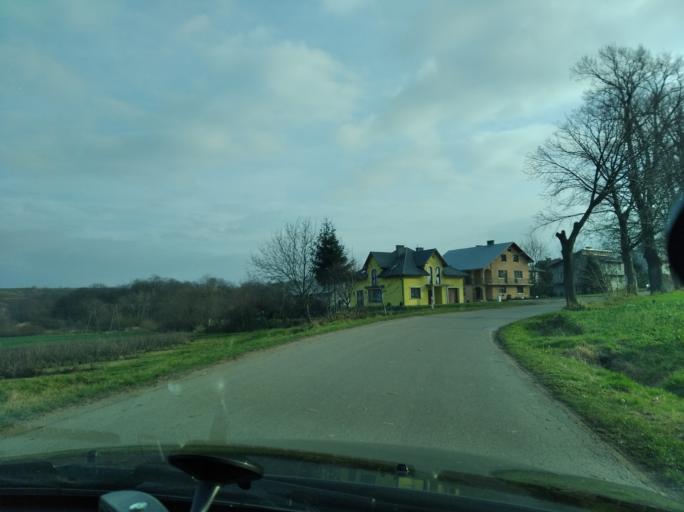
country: PL
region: Subcarpathian Voivodeship
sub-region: Powiat przeworski
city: Lopuszka Wielka
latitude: 49.9529
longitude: 22.4083
